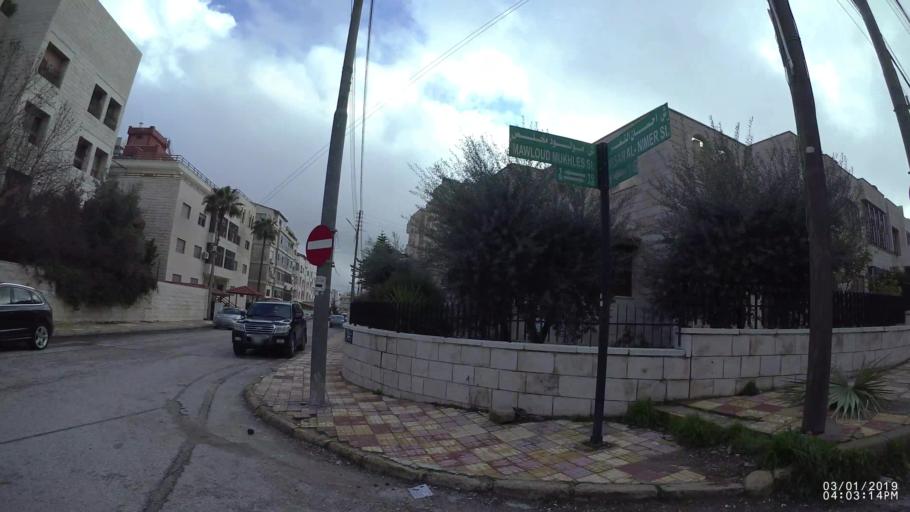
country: JO
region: Amman
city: Wadi as Sir
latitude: 31.9569
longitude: 35.8765
